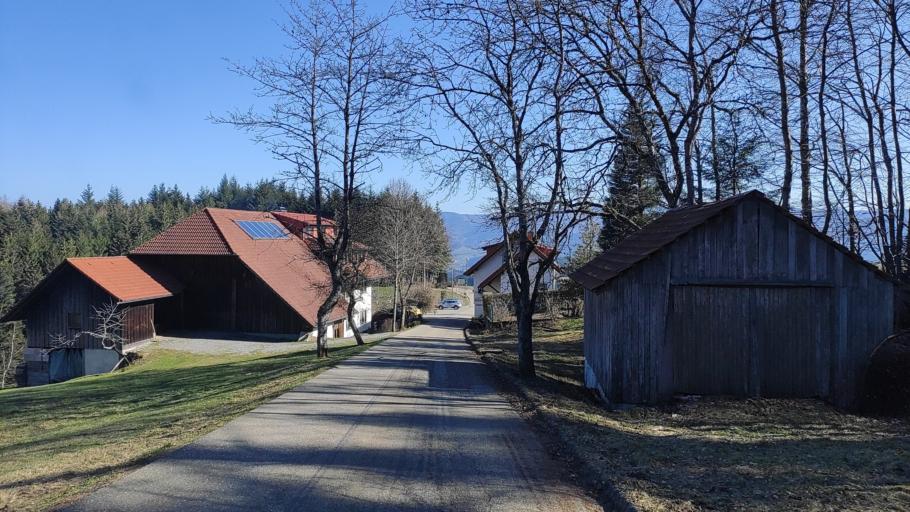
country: DE
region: Baden-Wuerttemberg
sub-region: Freiburg Region
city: Gutach im Breisgau
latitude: 48.1834
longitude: 7.9999
